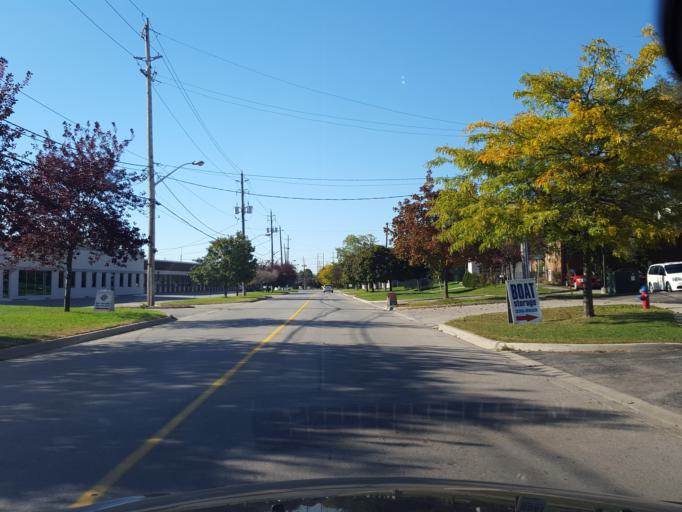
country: CA
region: Ontario
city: Burlington
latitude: 43.3518
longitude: -79.8104
